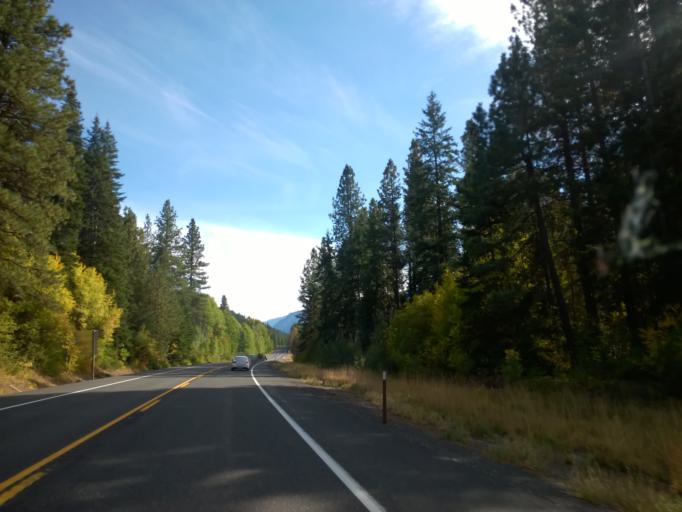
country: US
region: Washington
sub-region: Chelan County
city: Leavenworth
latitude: 47.7517
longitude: -120.7376
